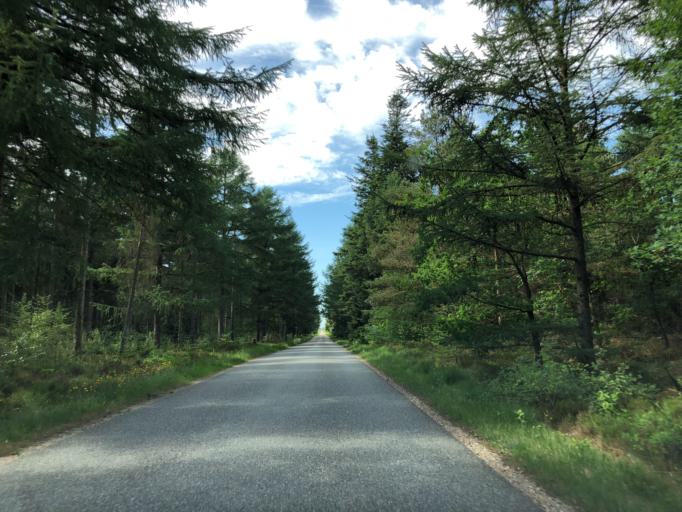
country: DK
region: Central Jutland
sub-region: Herning Kommune
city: Lind
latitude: 56.0419
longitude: 8.9347
